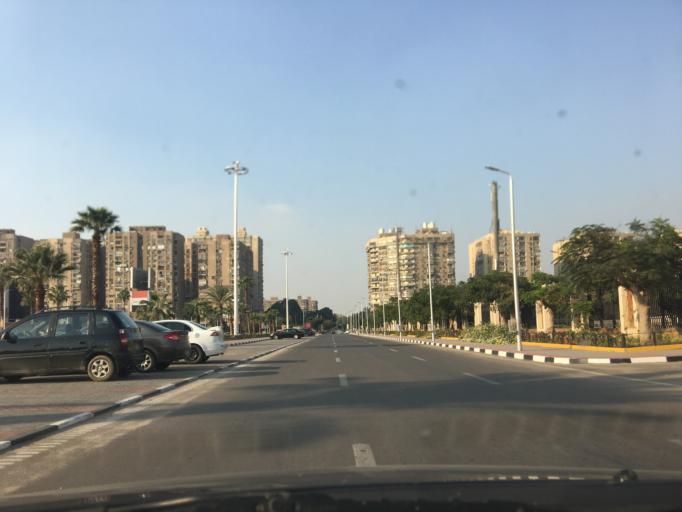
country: EG
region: Muhafazat al Qahirah
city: Cairo
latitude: 30.0740
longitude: 31.3102
